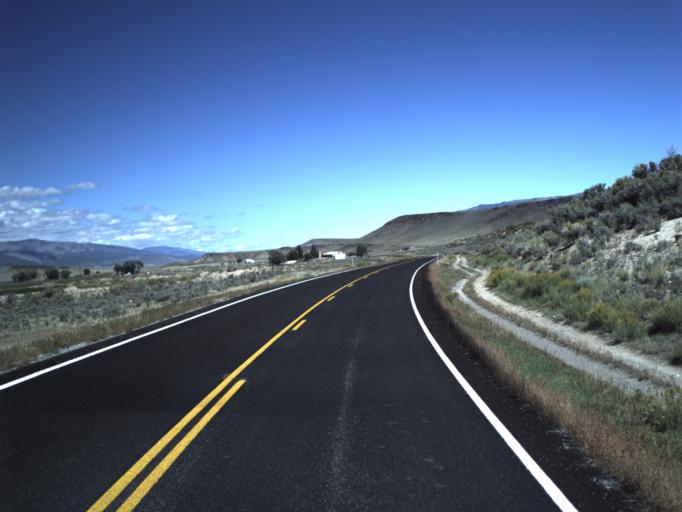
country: US
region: Utah
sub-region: Piute County
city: Junction
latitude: 38.1306
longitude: -112.0001
